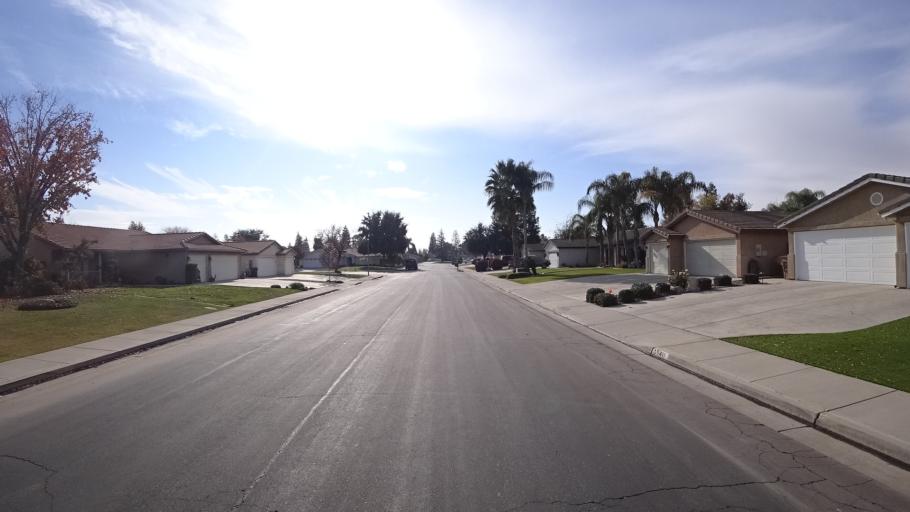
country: US
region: California
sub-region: Kern County
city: Greenacres
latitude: 35.4071
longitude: -119.0694
